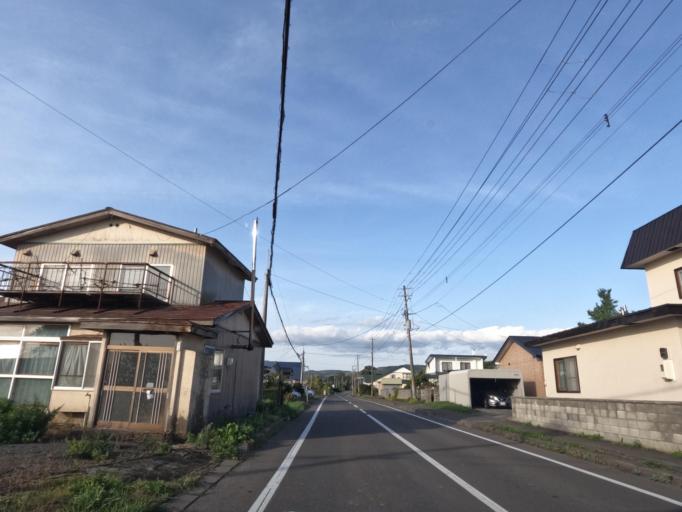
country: JP
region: Hokkaido
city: Date
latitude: 42.4670
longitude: 140.8845
